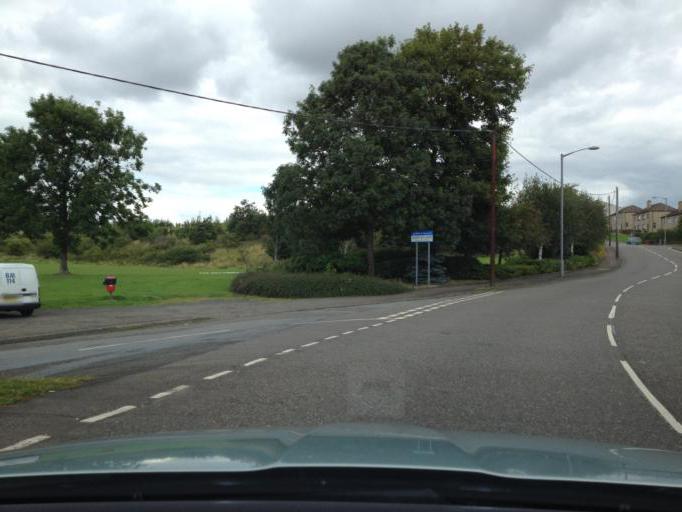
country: GB
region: Scotland
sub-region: Falkirk
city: Falkirk
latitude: 55.9842
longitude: -3.7880
